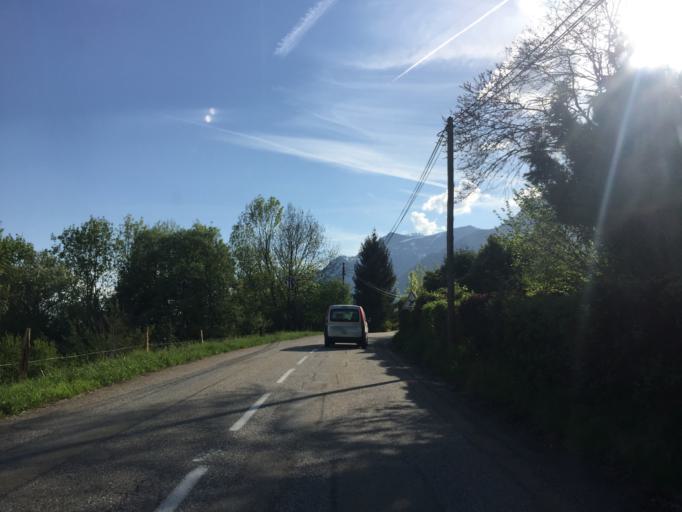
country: FR
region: Rhone-Alpes
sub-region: Departement de la Savoie
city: Mercury
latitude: 45.6638
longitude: 6.3131
